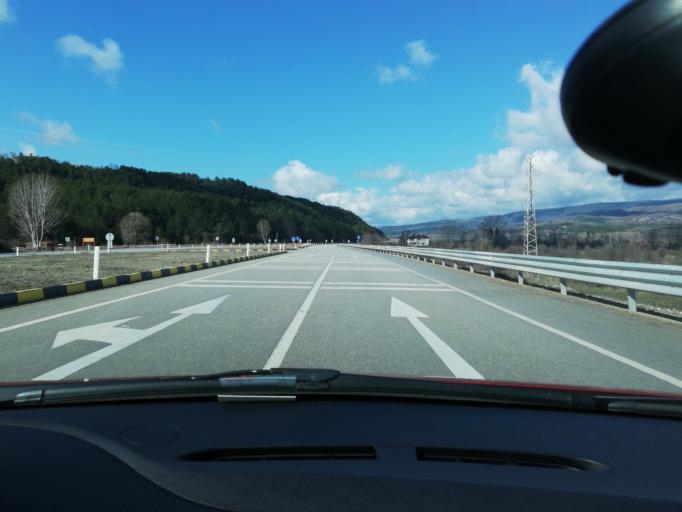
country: TR
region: Kastamonu
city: Arac
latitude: 41.2279
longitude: 33.2816
